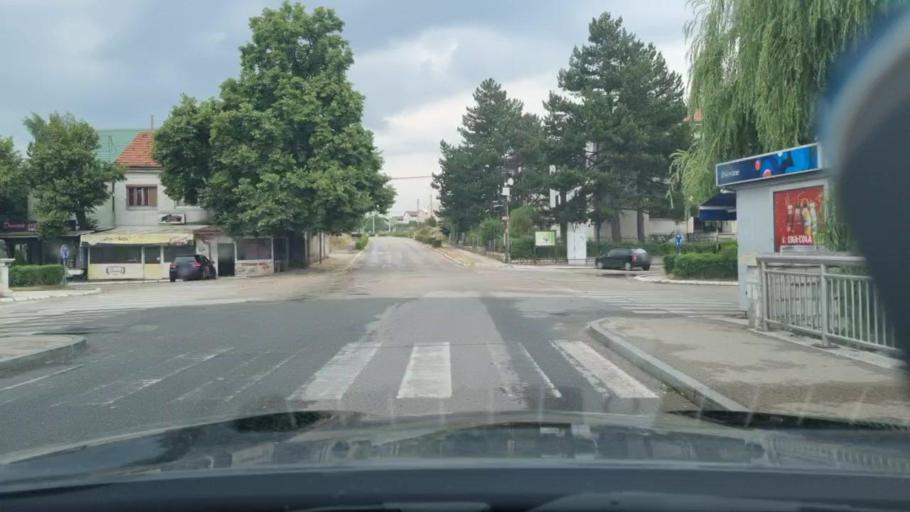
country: BA
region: Federation of Bosnia and Herzegovina
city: Livno
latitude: 43.8274
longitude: 17.0039
